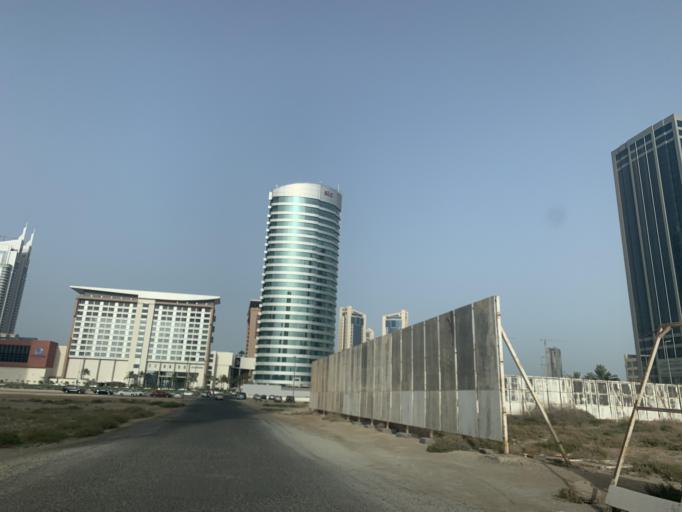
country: BH
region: Manama
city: Jidd Hafs
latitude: 26.2327
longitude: 50.5483
